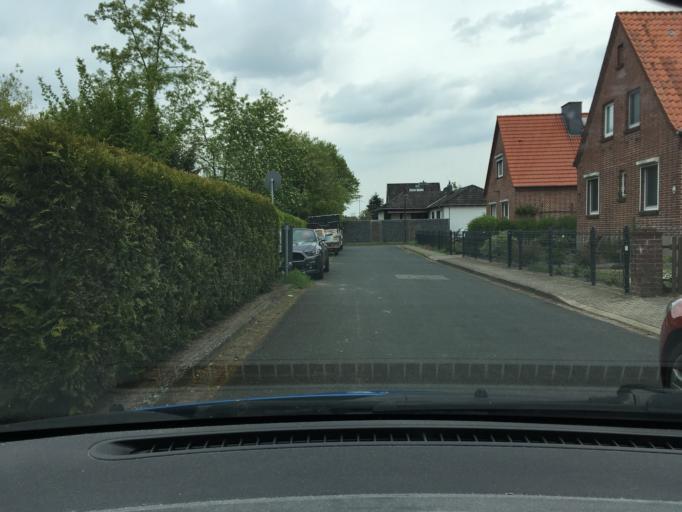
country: DE
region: Lower Saxony
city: Bardowick
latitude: 53.2882
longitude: 10.3698
